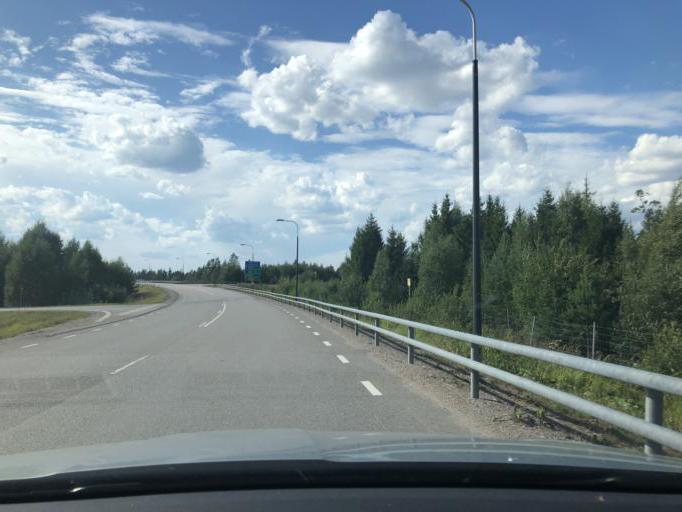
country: SE
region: Uppsala
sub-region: Tierps Kommun
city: Tierp
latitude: 60.2149
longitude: 17.5004
